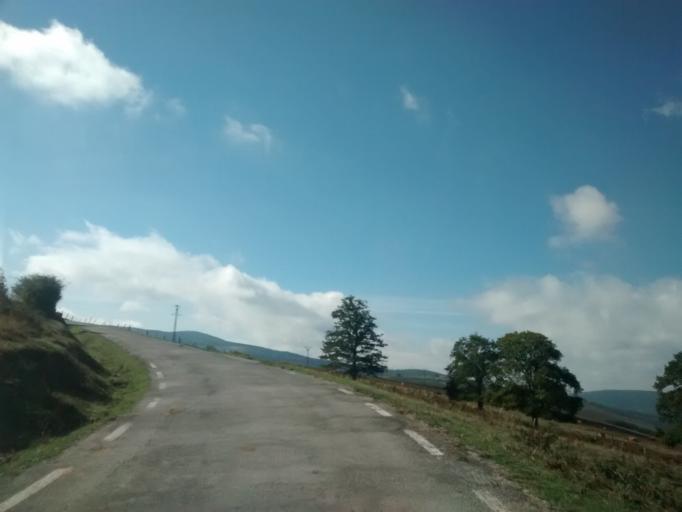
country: ES
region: Castille and Leon
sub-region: Provincia de Burgos
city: Arija
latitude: 42.9239
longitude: -3.9924
